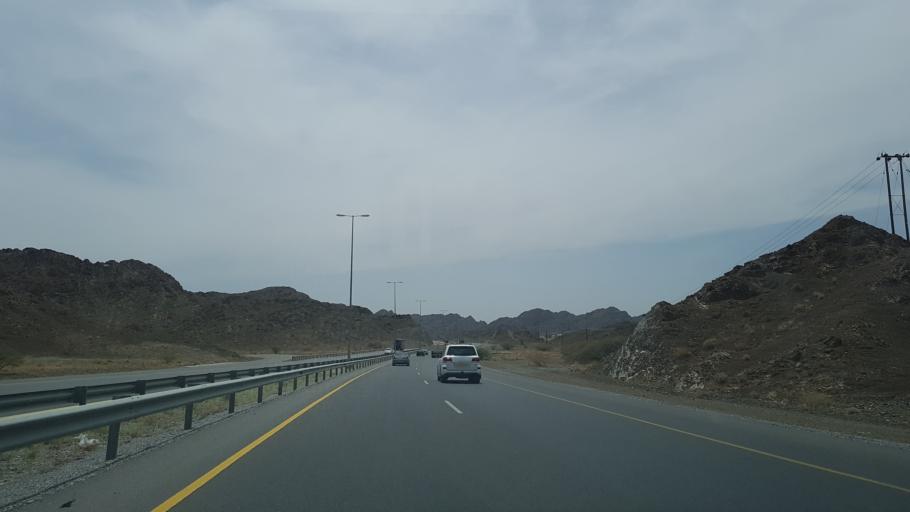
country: OM
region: Muhafazat ad Dakhiliyah
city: Izki
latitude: 22.9472
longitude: 57.7900
